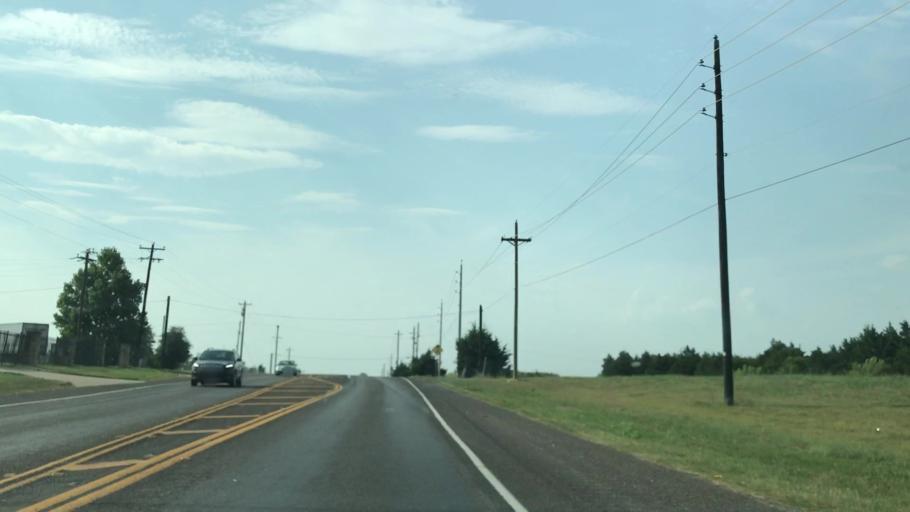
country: US
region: Texas
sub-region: Rockwall County
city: Rockwall
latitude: 32.8976
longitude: -96.4422
